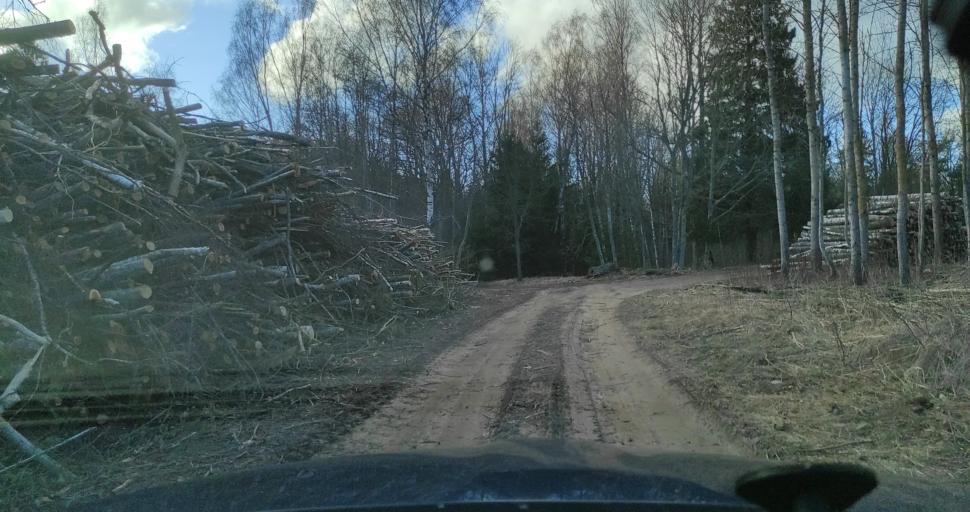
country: LV
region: Aizpute
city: Aizpute
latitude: 56.8707
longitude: 21.7552
